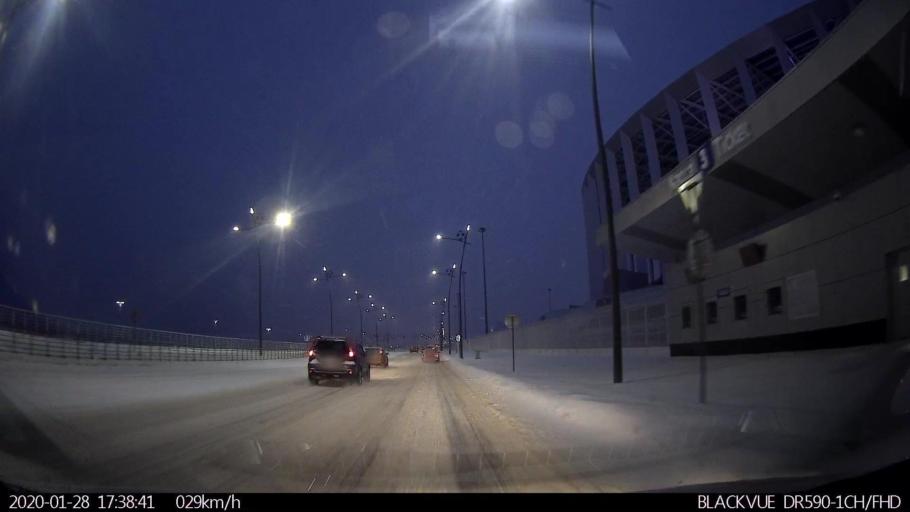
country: RU
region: Nizjnij Novgorod
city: Nizhniy Novgorod
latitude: 56.3394
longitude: 43.9639
